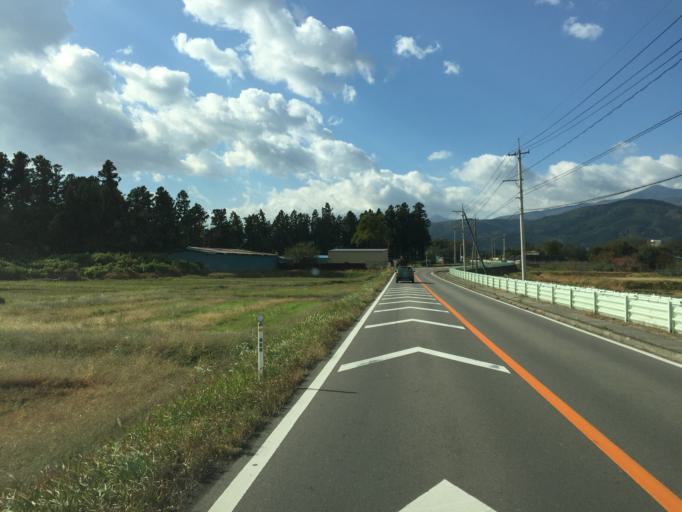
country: JP
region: Fukushima
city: Fukushima-shi
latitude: 37.7631
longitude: 140.3789
